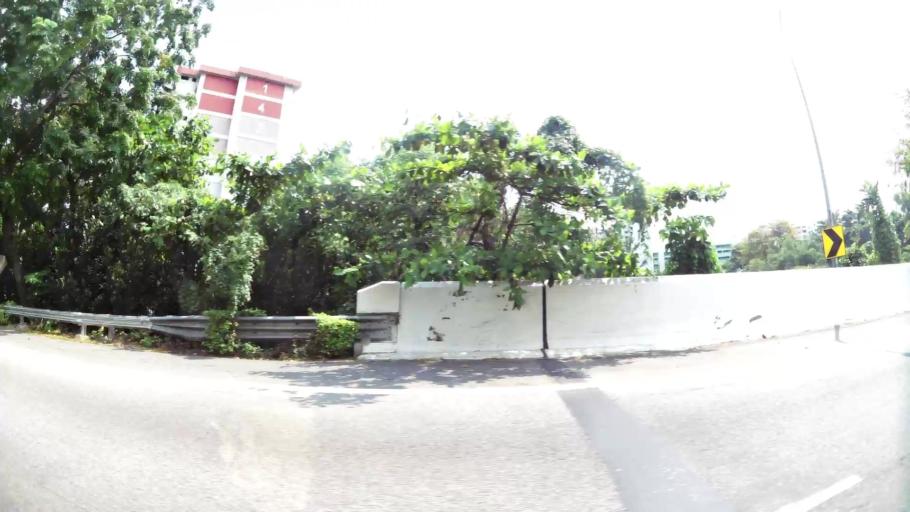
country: SG
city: Singapore
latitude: 1.2773
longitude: 103.8272
